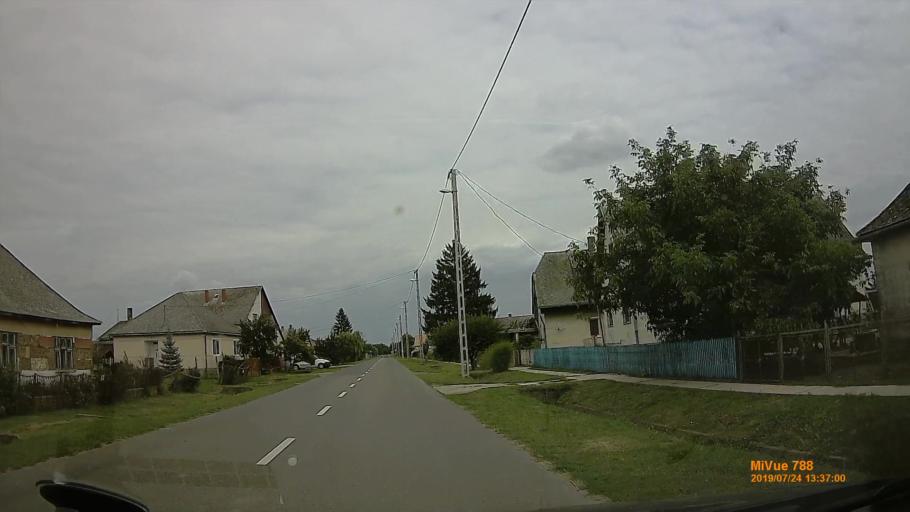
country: HU
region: Szabolcs-Szatmar-Bereg
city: Aranyosapati
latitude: 48.2274
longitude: 22.2968
